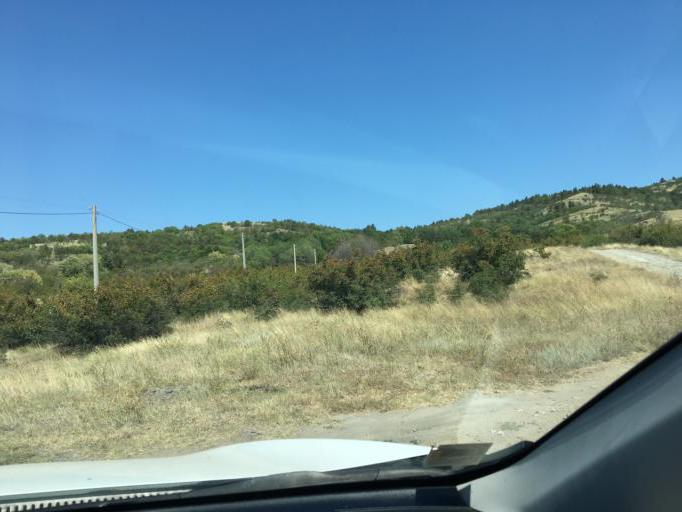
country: BG
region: Burgas
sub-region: Obshtina Kameno
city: Kameno
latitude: 42.6335
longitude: 27.3890
